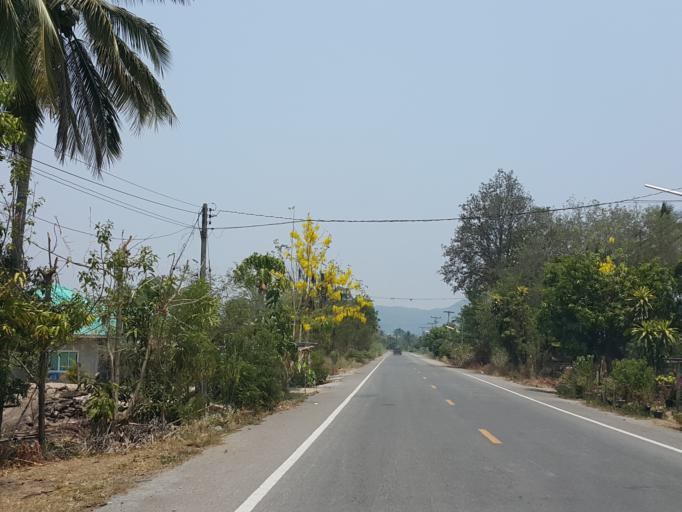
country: TH
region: Kamphaeng Phet
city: Pang Sila Thong
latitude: 16.0547
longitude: 99.3562
